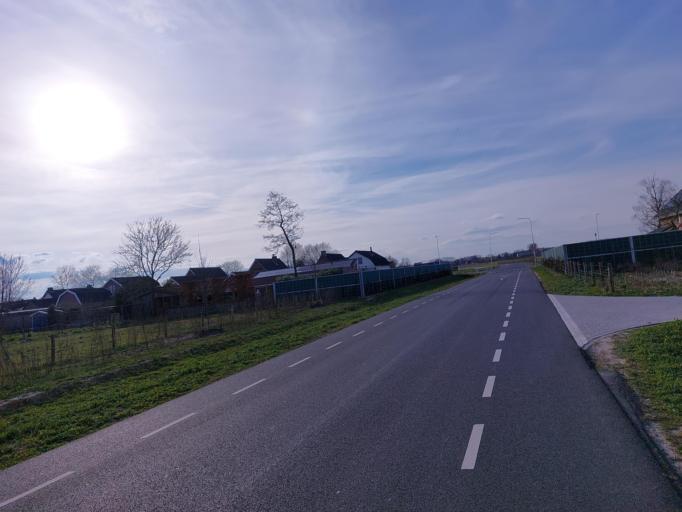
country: NL
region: Gelderland
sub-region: Gemeente Geldermalsen
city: Geldermalsen
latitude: 51.8933
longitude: 5.2747
